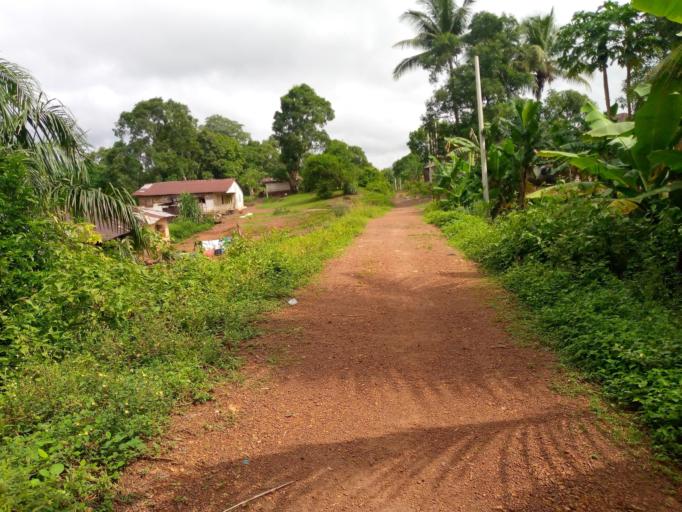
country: SL
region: Southern Province
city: Moyamba
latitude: 8.1583
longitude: -12.4334
